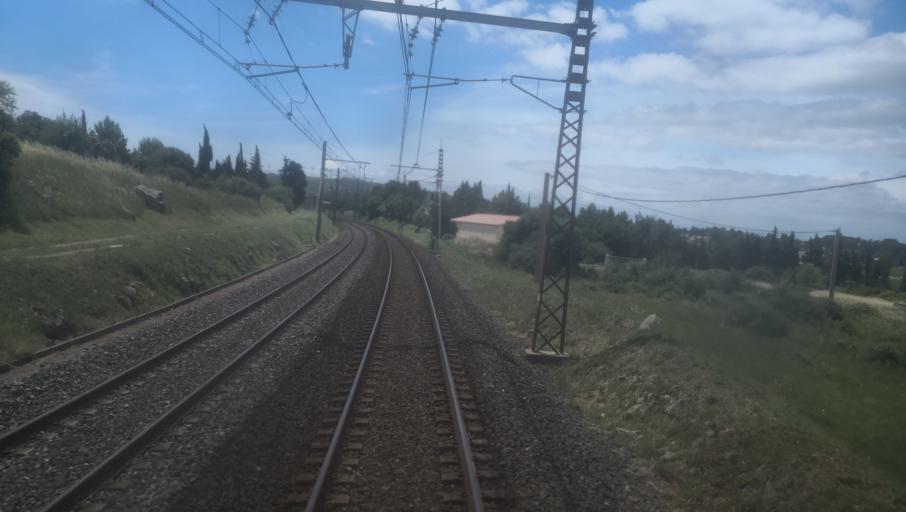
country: FR
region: Languedoc-Roussillon
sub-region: Departement de l'Aude
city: Nevian
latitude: 43.2147
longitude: 2.9136
